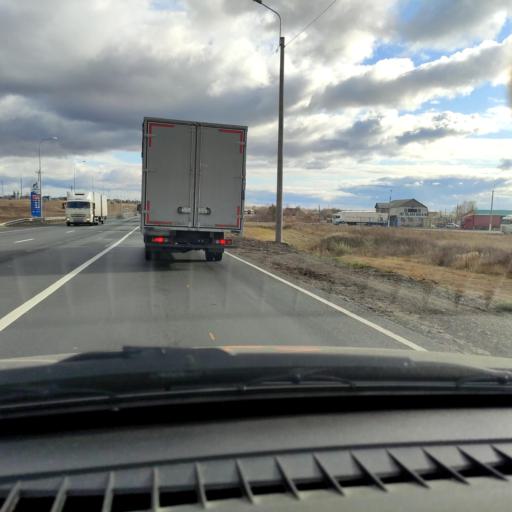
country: RU
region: Samara
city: Syzran'
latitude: 53.2106
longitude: 48.4825
